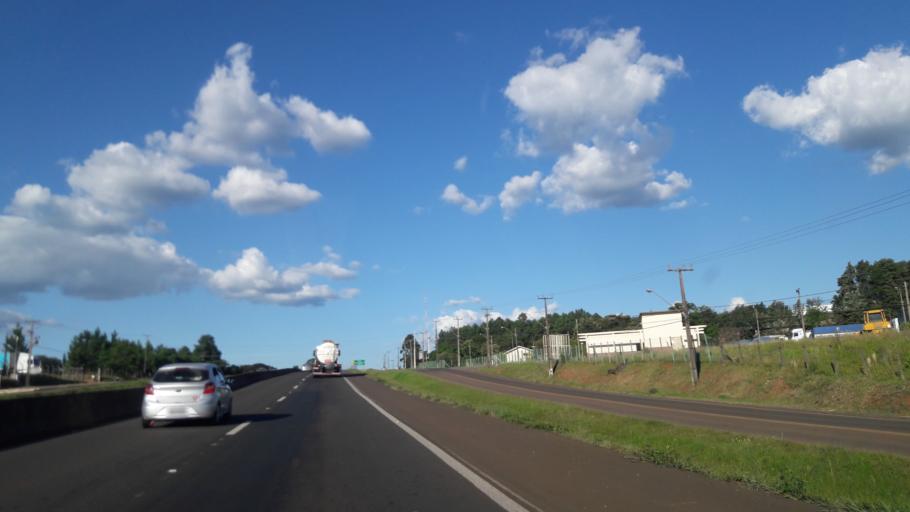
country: BR
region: Parana
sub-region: Guarapuava
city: Guarapuava
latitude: -25.3518
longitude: -51.4581
